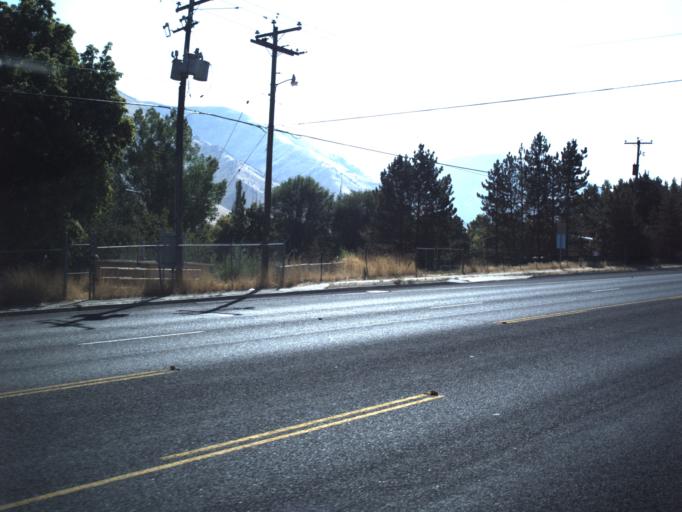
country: US
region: Utah
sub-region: Cache County
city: Nibley
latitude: 41.6600
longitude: -111.8335
